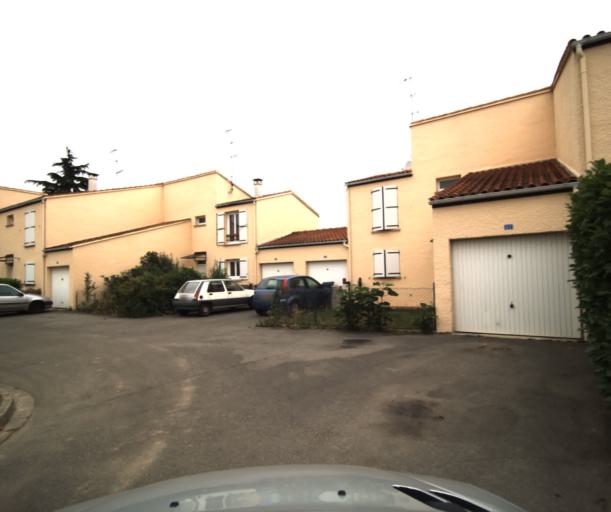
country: FR
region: Midi-Pyrenees
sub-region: Departement de la Haute-Garonne
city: Portet-sur-Garonne
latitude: 43.5433
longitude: 1.4082
